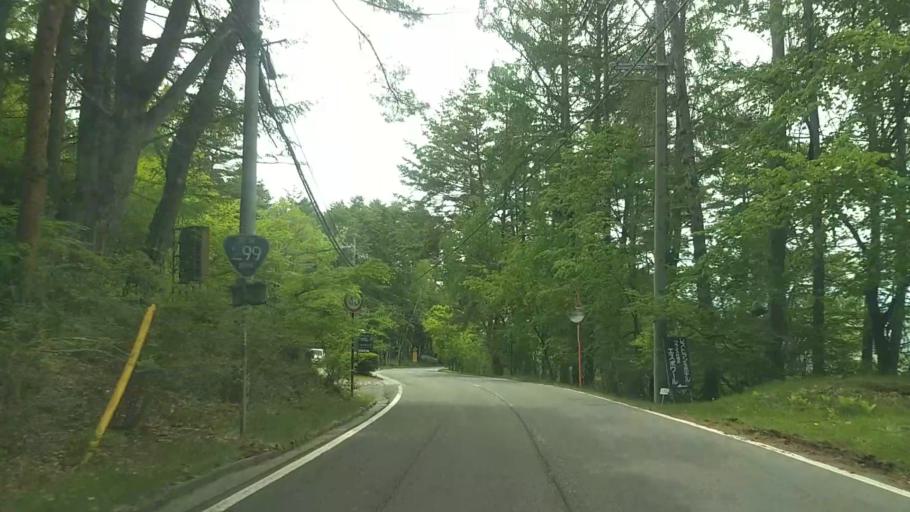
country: JP
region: Nagano
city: Chino
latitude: 36.0457
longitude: 138.2693
